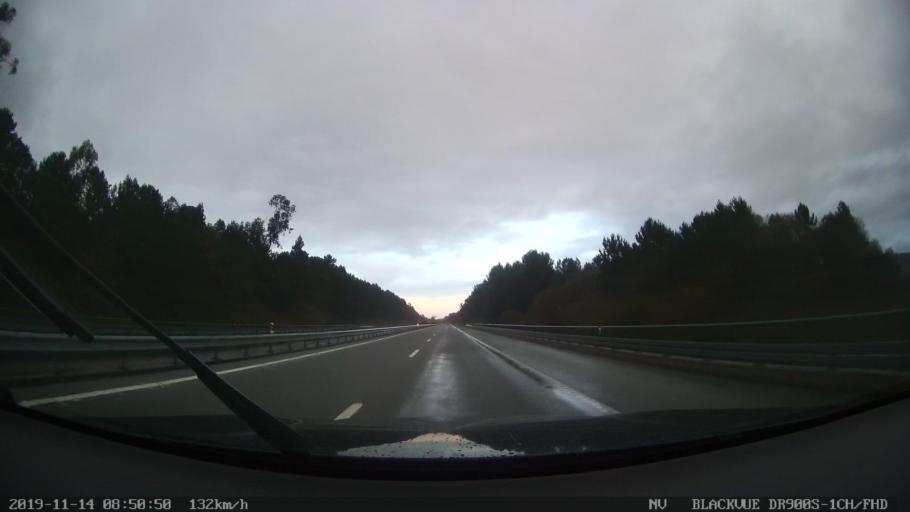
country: PT
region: Viana do Castelo
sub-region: Vila Nova de Cerveira
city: Vila Nova de Cerveira
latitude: 41.8960
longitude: -8.6589
